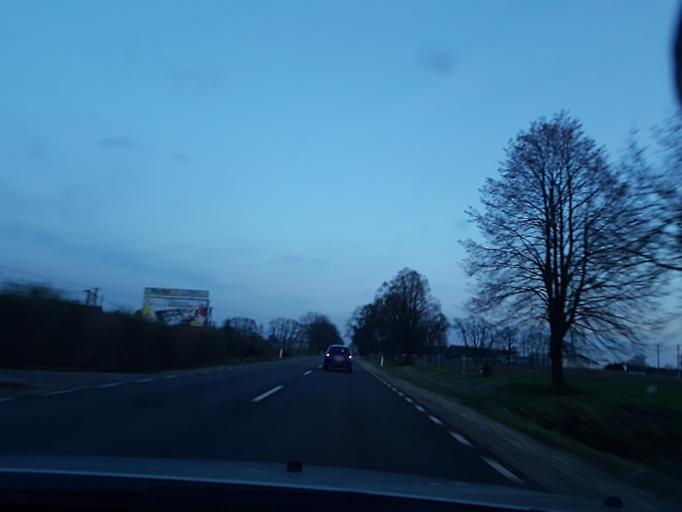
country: PL
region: Masovian Voivodeship
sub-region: Powiat plocki
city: Wyszogrod
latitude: 52.4080
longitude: 20.1374
